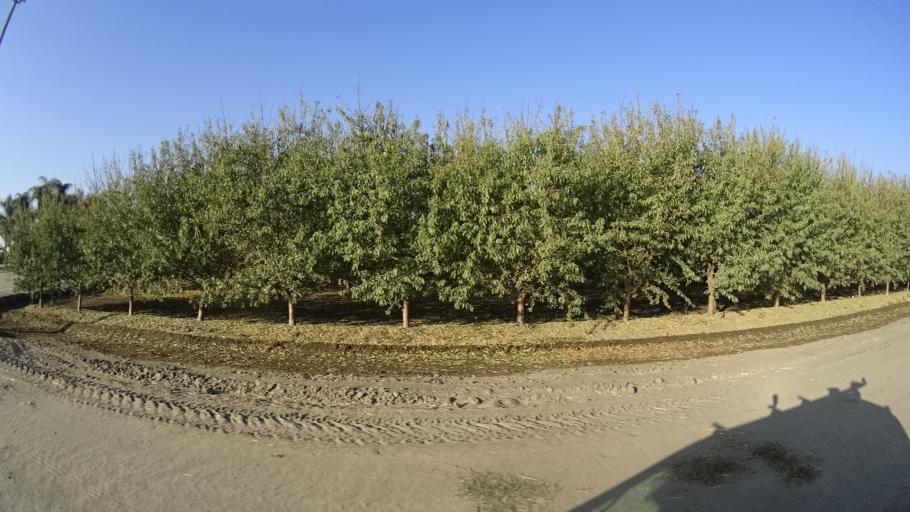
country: US
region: California
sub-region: Kern County
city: Greenfield
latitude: 35.2447
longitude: -118.9854
